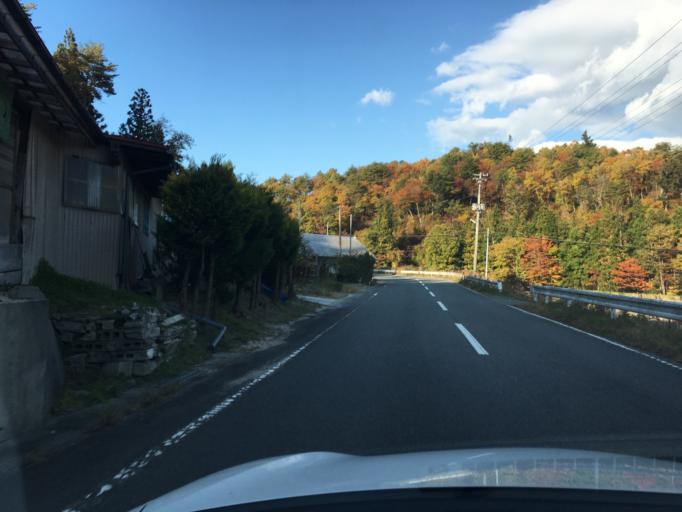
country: JP
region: Fukushima
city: Iwaki
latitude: 37.2688
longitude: 140.7646
